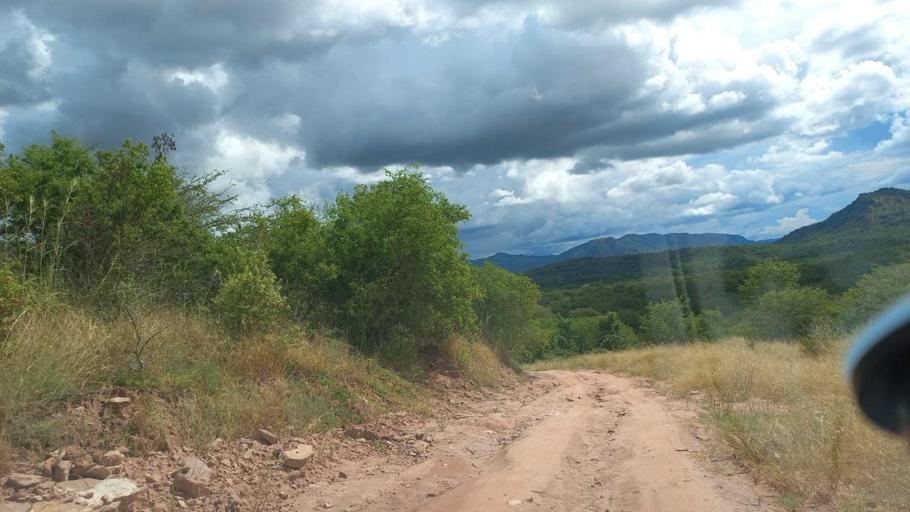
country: ZM
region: Lusaka
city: Luangwa
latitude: -15.6358
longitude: 30.3842
